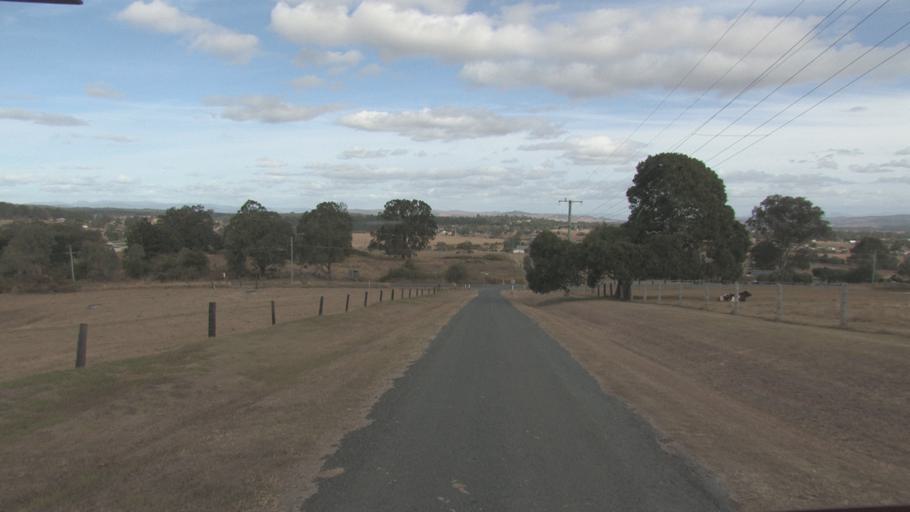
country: AU
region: Queensland
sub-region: Logan
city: Cedar Vale
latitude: -27.9144
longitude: 152.9961
